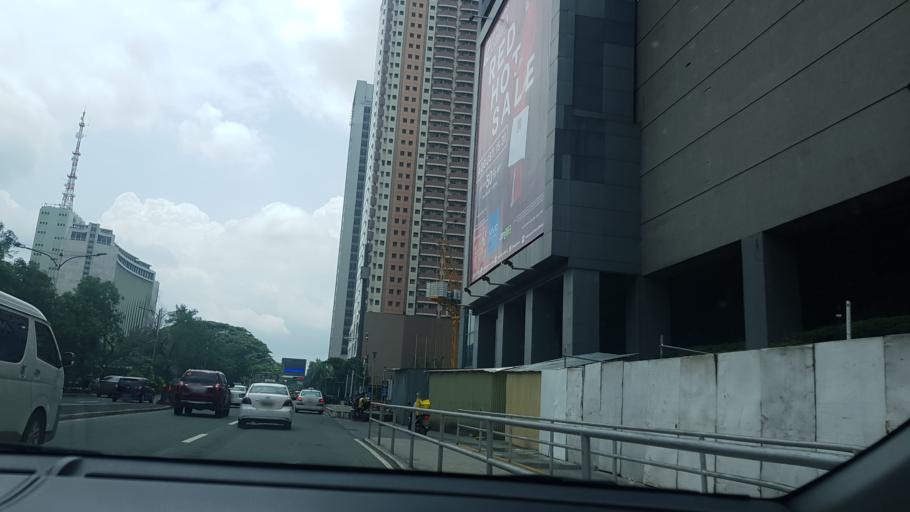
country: PH
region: Metro Manila
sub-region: Pasig
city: Pasig City
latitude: 14.5913
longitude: 121.0605
